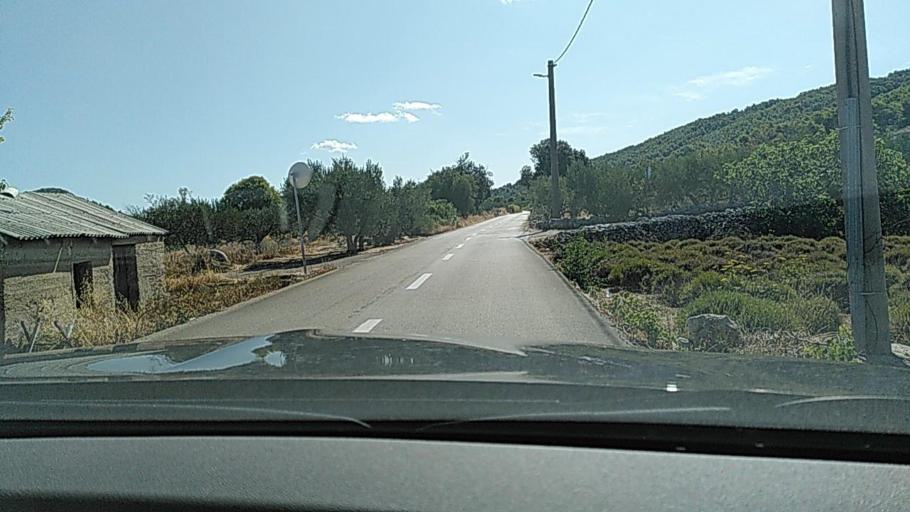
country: HR
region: Splitsko-Dalmatinska
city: Jelsa
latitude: 43.1457
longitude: 16.8343
